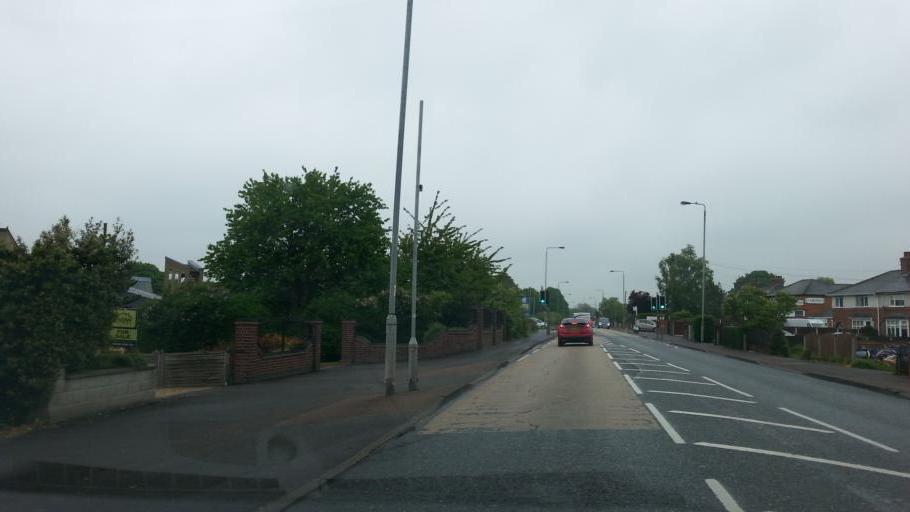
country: GB
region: England
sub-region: Nottinghamshire
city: Newark on Trent
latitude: 53.0881
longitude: -0.7949
